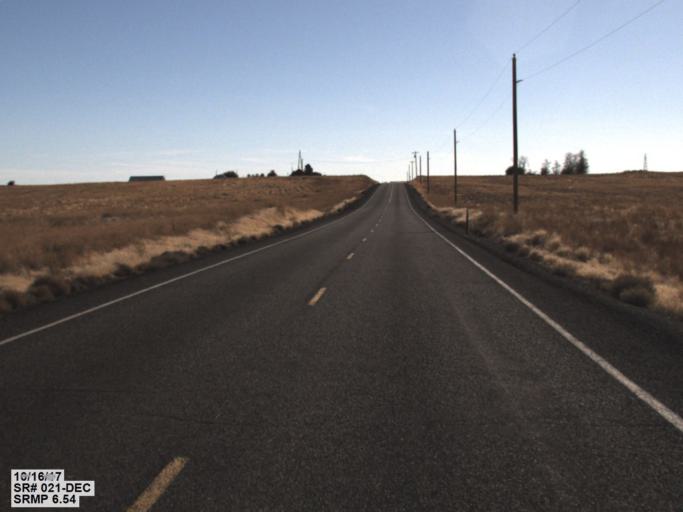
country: US
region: Washington
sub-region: Franklin County
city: Connell
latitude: 46.7209
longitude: -118.5481
